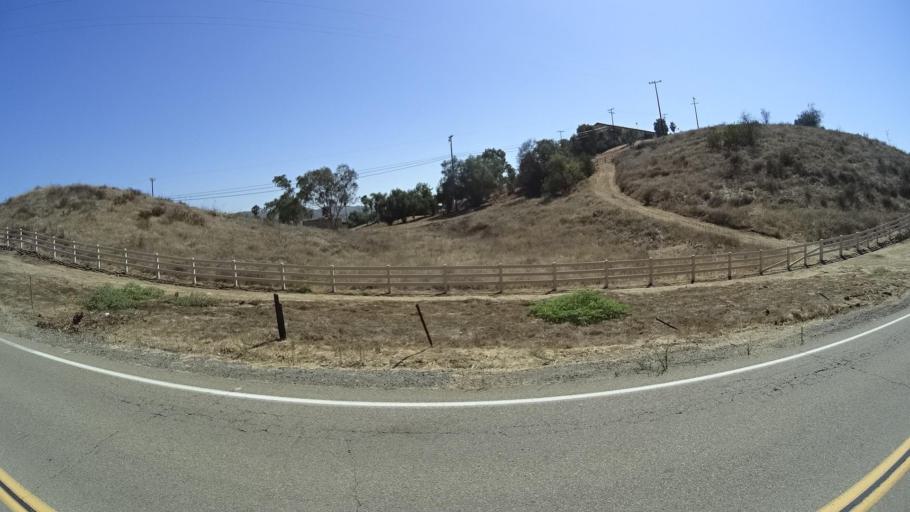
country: US
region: California
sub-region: San Diego County
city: Bonsall
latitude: 33.2975
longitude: -117.2073
